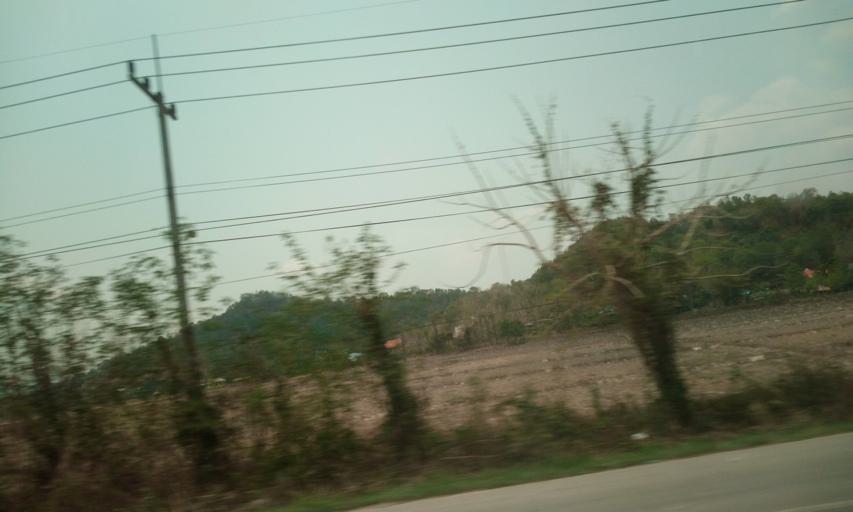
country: TH
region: Chiang Rai
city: Thoeng
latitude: 19.6898
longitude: 100.1454
